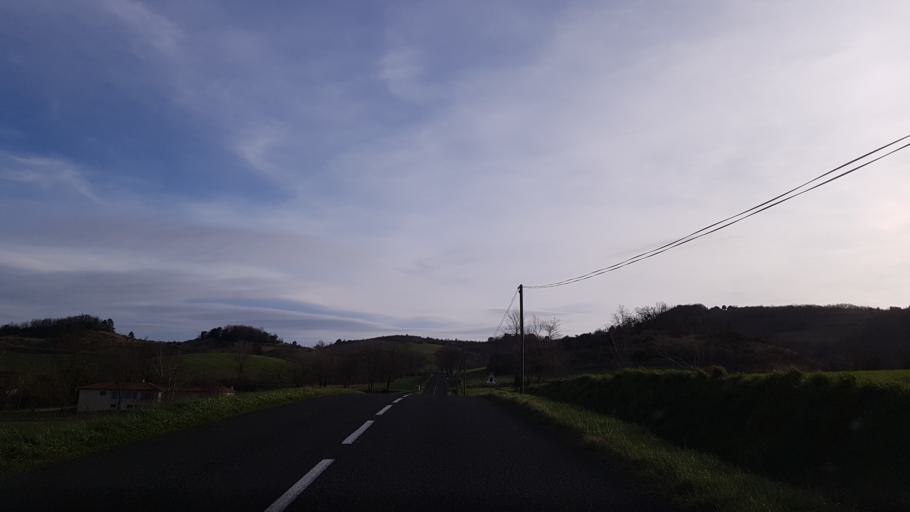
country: FR
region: Midi-Pyrenees
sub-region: Departement de l'Ariege
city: Mirepoix
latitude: 43.1392
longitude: 1.9117
